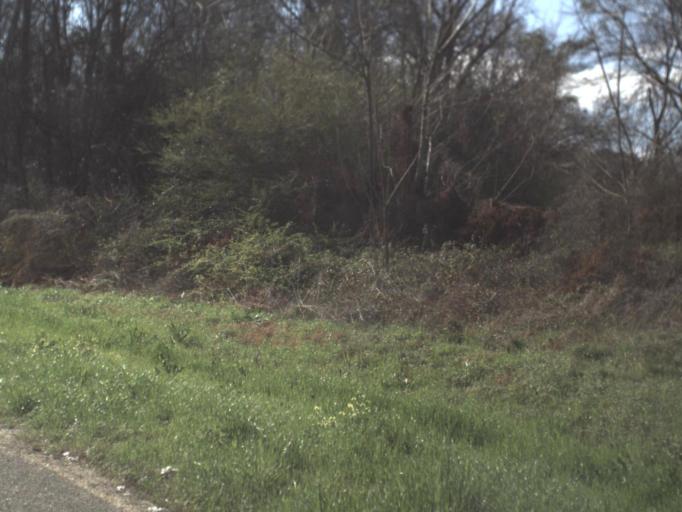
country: US
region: Florida
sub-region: Jackson County
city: Malone
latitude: 30.9981
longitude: -85.2004
